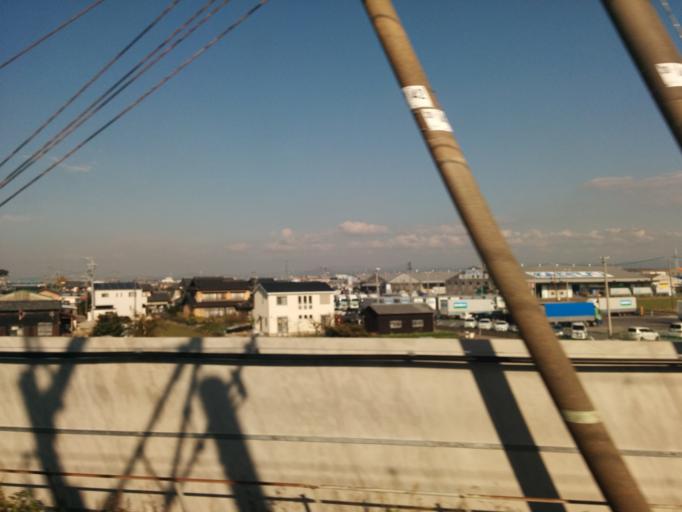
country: JP
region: Aichi
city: Okazaki
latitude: 34.9034
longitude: 137.1210
